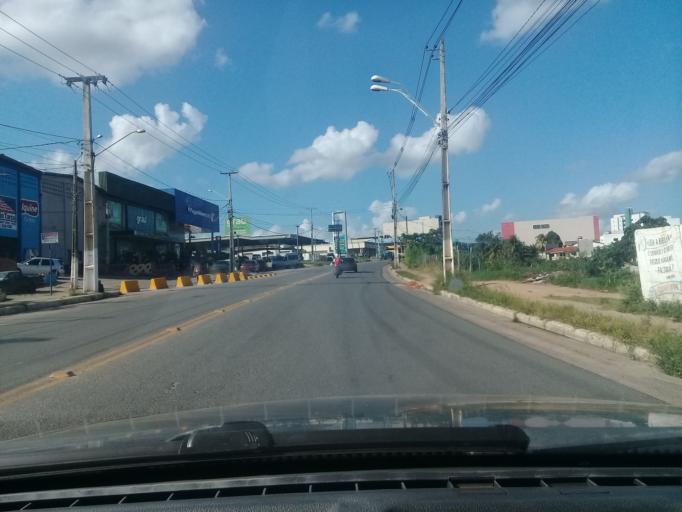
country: BR
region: Pernambuco
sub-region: Vitoria De Santo Antao
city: Vitoria de Santo Antao
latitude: -8.1154
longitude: -35.2959
